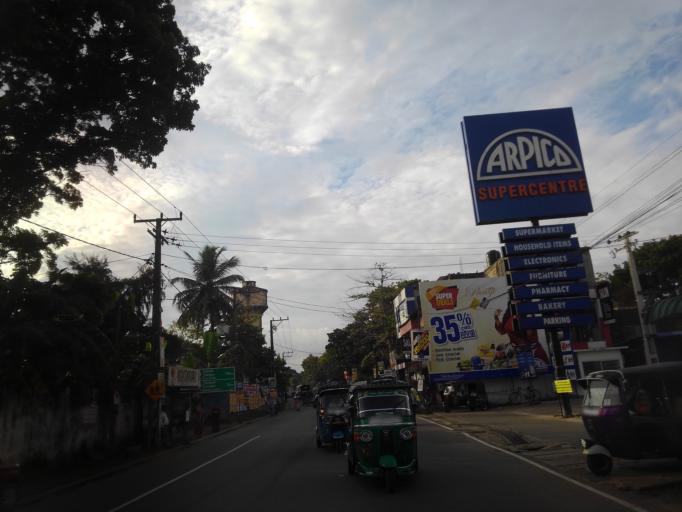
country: LK
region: Southern
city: Galle
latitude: 6.0366
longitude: 80.2300
